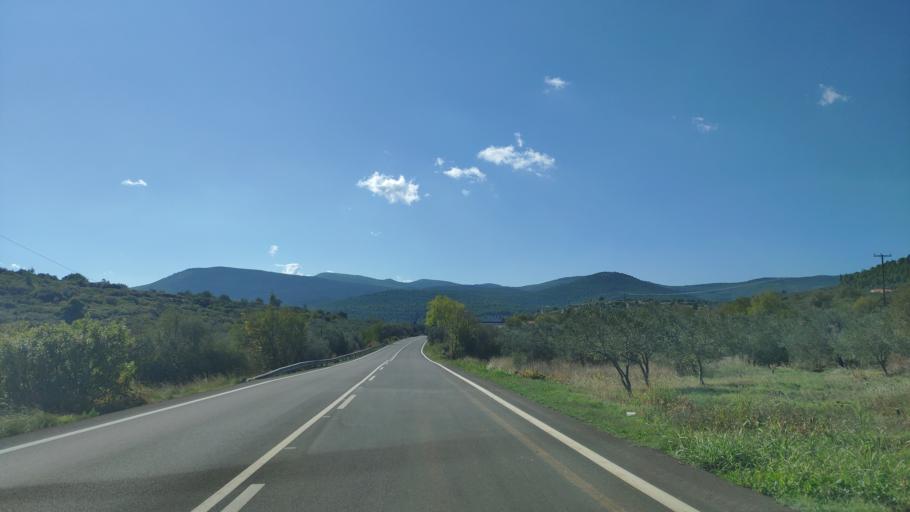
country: GR
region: Peloponnese
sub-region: Nomos Korinthias
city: Sofikon
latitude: 37.8050
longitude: 23.0817
